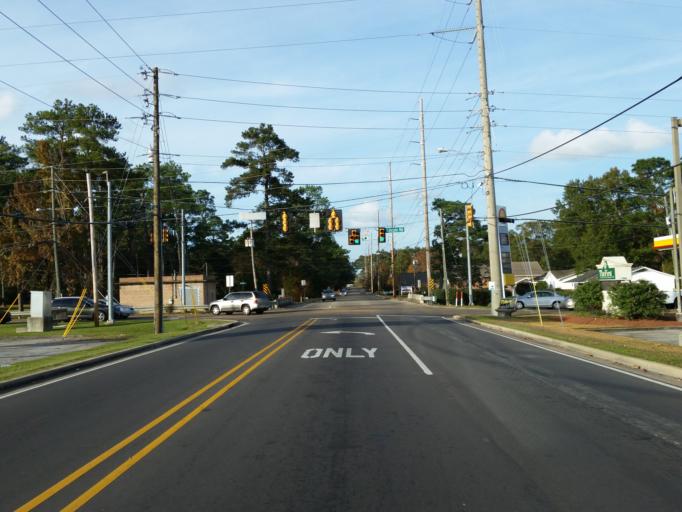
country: US
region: Mississippi
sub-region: Lamar County
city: West Hattiesburg
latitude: 31.3036
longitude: -89.3312
